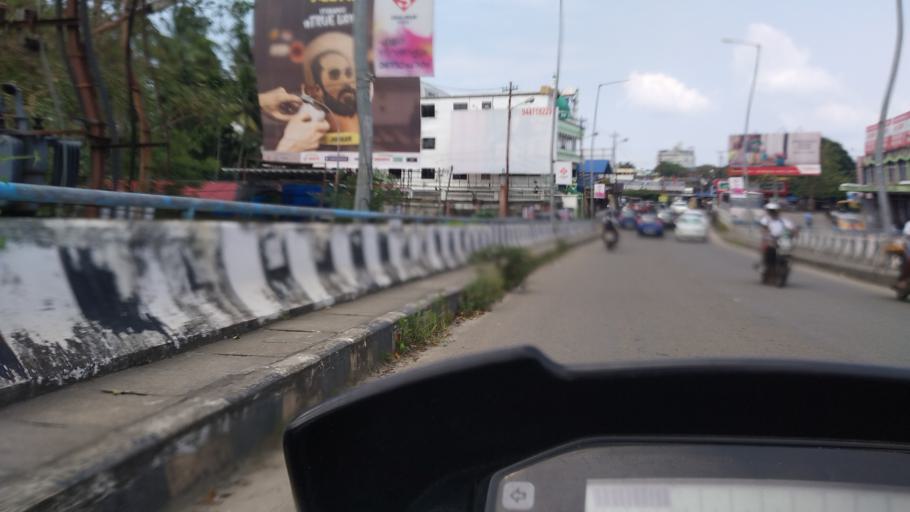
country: IN
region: Kerala
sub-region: Ernakulam
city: Cochin
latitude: 9.9772
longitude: 76.2886
